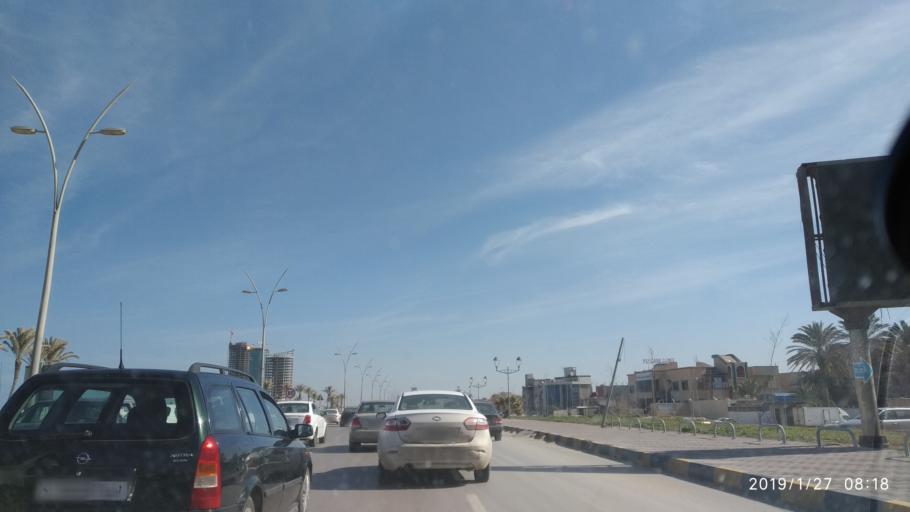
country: LY
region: Tripoli
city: Tripoli
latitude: 32.9066
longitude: 13.2553
